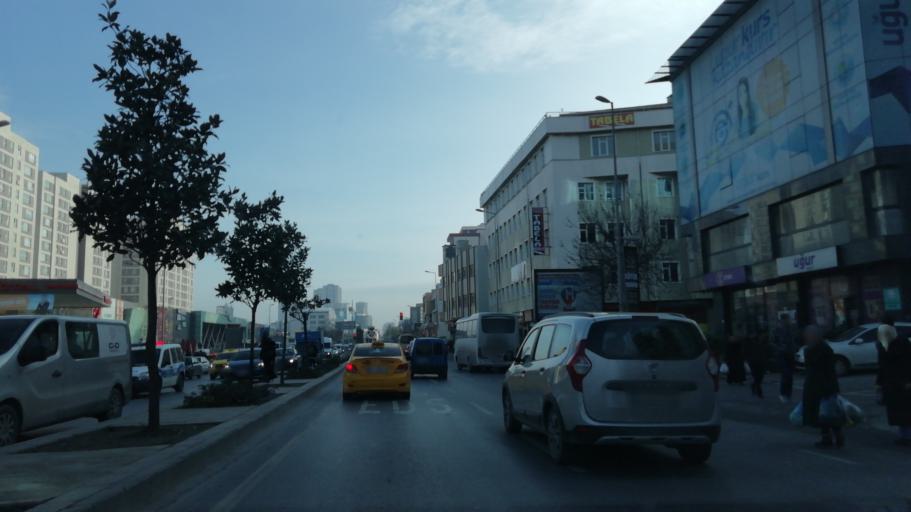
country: TR
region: Istanbul
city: Esenyurt
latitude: 41.0427
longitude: 28.6759
